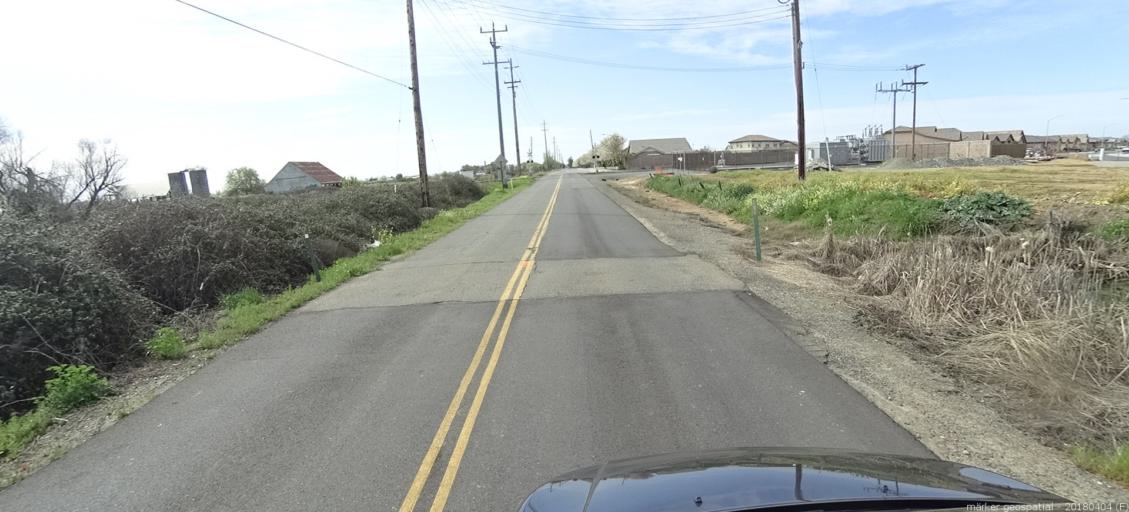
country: US
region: California
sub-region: Sacramento County
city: Galt
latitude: 38.2756
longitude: -121.2826
